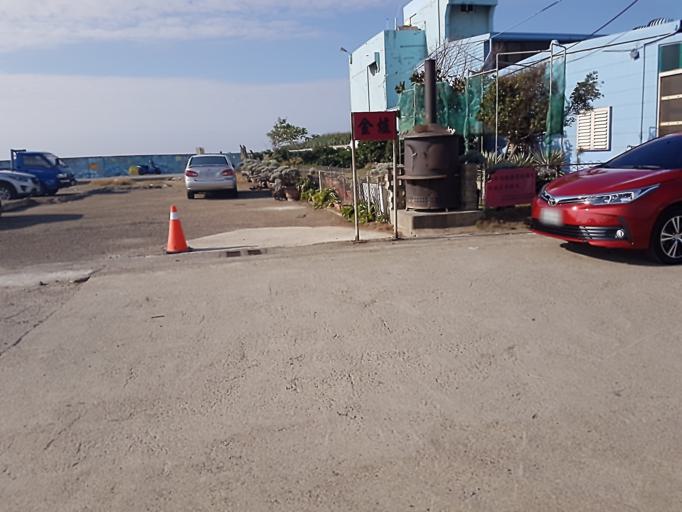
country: TW
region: Taiwan
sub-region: Hsinchu
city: Hsinchu
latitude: 24.8495
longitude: 120.9213
